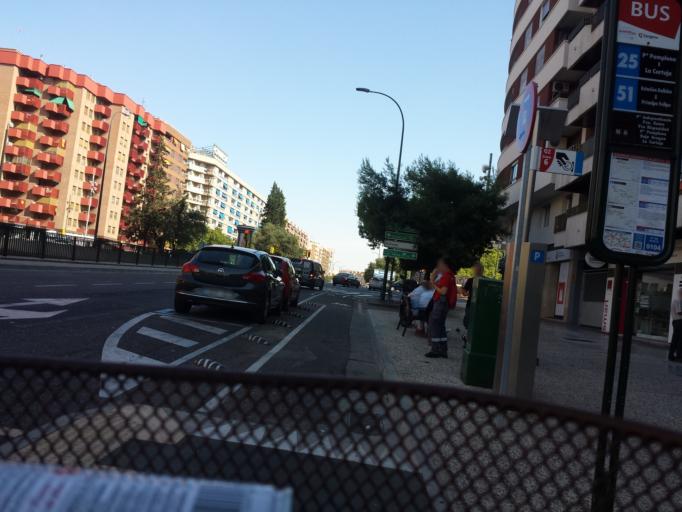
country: ES
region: Aragon
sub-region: Provincia de Zaragoza
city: Zaragoza
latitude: 41.6454
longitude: -0.8783
